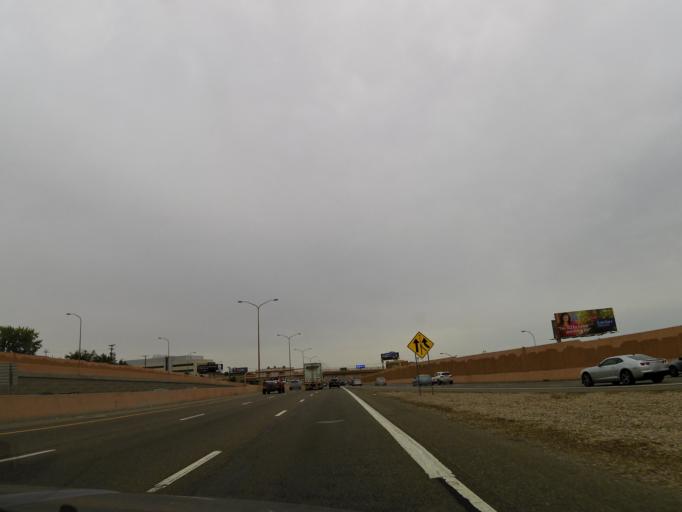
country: US
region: New Mexico
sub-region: Bernalillo County
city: Albuquerque
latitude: 35.1012
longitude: -106.6316
